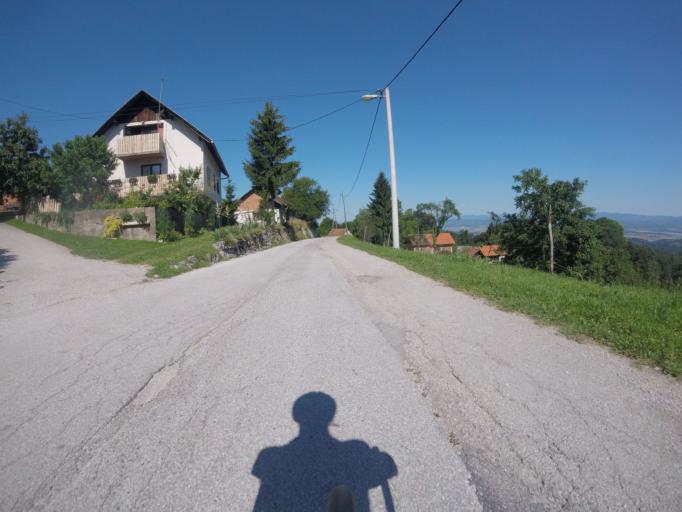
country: SI
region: Brezice
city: Brezice
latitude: 45.8395
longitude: 15.5697
